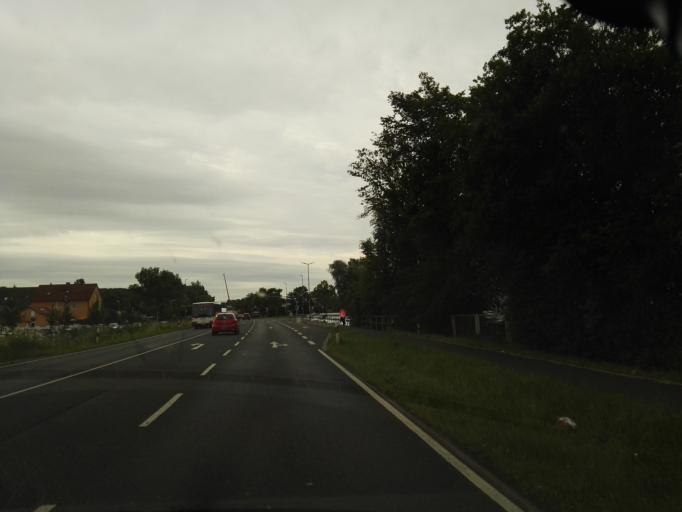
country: DE
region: Bavaria
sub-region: Upper Franconia
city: Burgkunstadt
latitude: 50.1402
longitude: 11.2442
